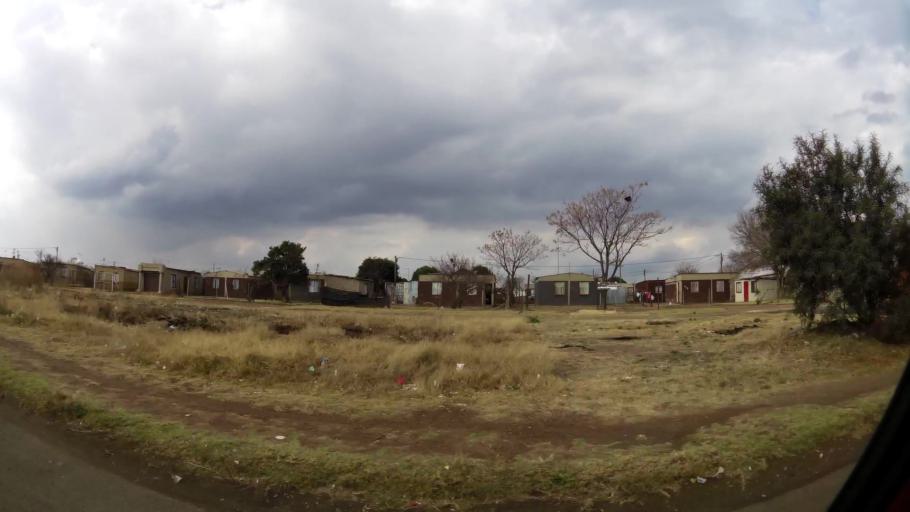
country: ZA
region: Gauteng
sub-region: Sedibeng District Municipality
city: Vanderbijlpark
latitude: -26.6889
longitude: 27.7843
